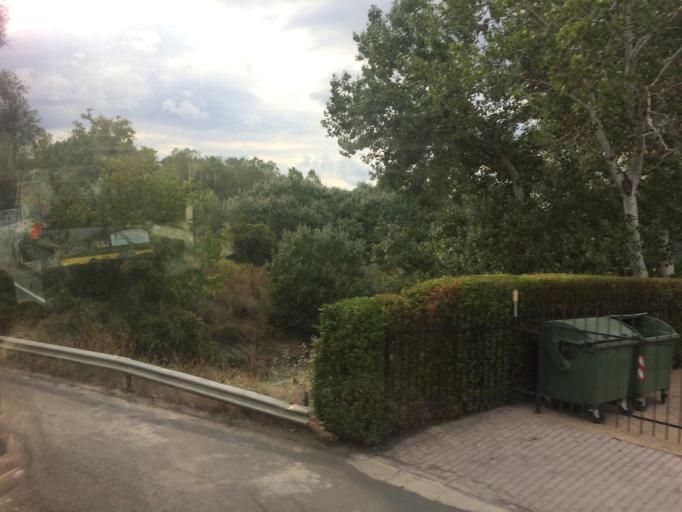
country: BG
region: Burgas
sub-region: Obshtina Nesebur
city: Sveti Vlas
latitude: 42.7103
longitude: 27.7248
